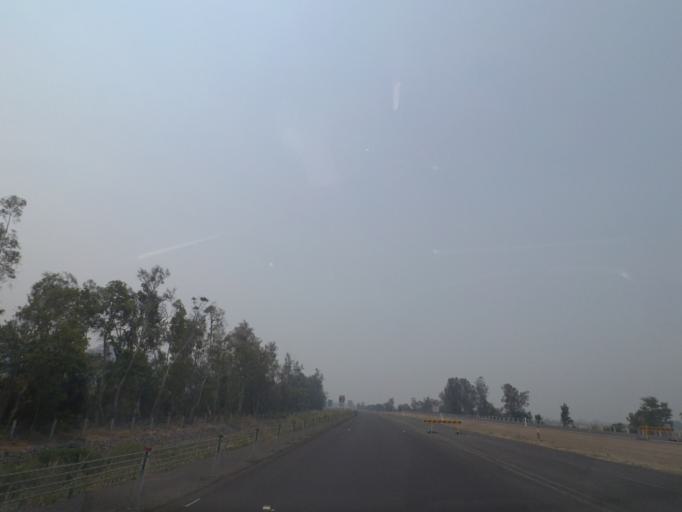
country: AU
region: New South Wales
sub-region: Ballina
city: Ballina
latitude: -28.8791
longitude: 153.4870
